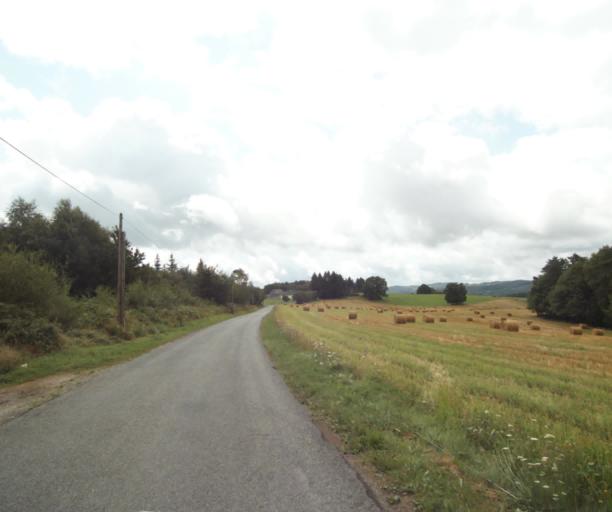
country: FR
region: Limousin
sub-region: Departement de la Correze
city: Sainte-Fortunade
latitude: 45.1724
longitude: 1.8026
